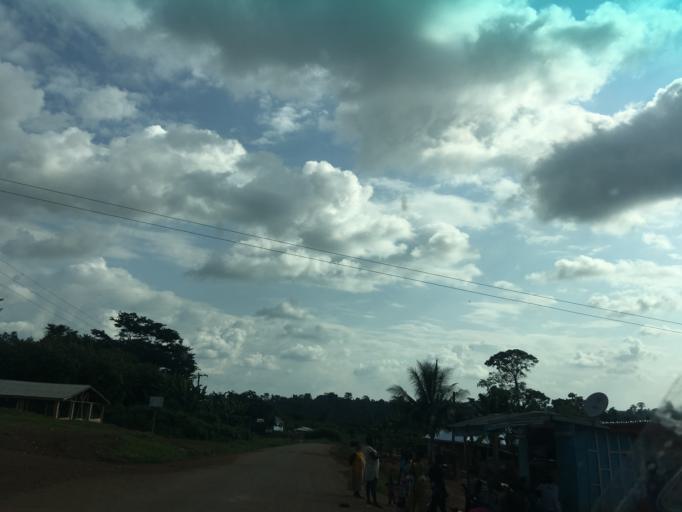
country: GH
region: Western
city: Bibiani
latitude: 6.7846
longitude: -2.5444
